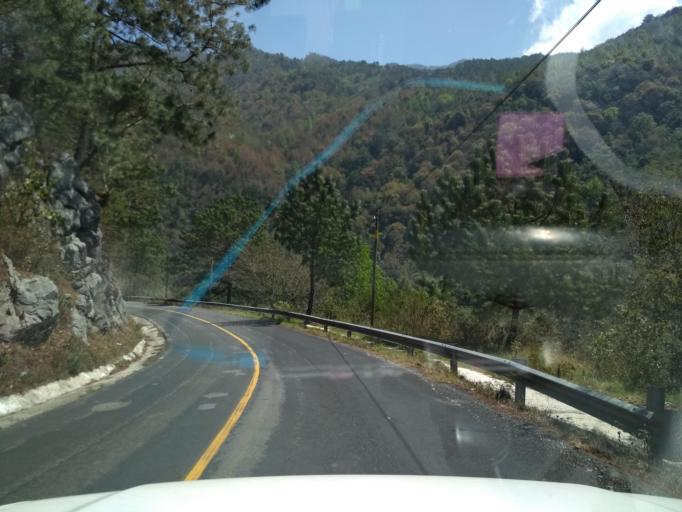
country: MX
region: Veracruz
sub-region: Tlilapan
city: Tonalixco
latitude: 18.7638
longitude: -97.0813
